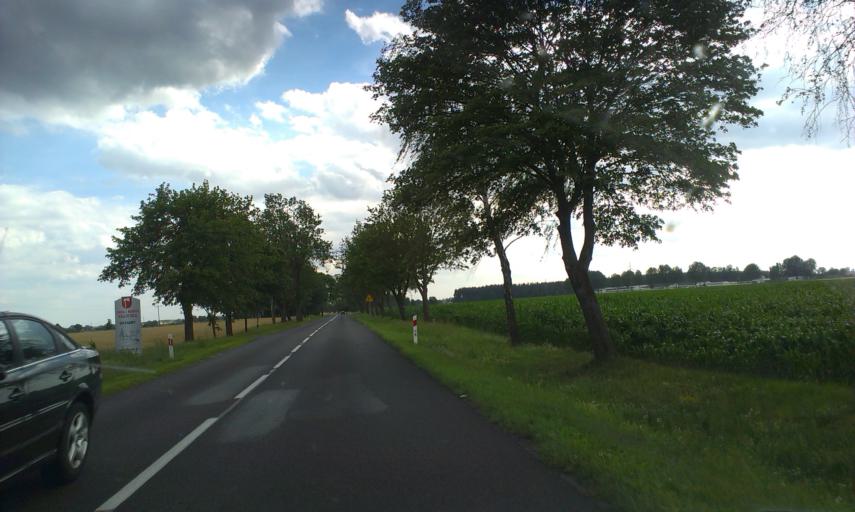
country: PL
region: Greater Poland Voivodeship
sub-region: Powiat zlotowski
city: Krajenka
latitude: 53.3249
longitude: 16.9999
